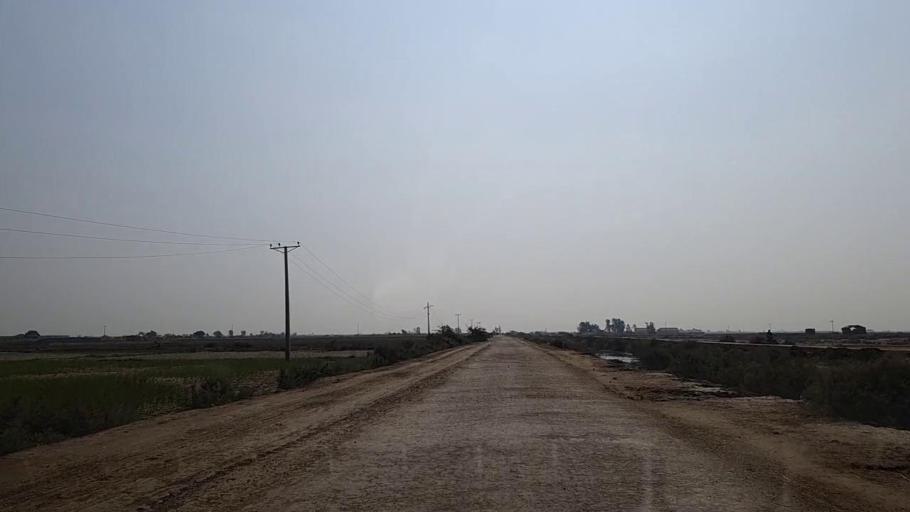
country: PK
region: Sindh
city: Thatta
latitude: 24.7155
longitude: 67.7684
